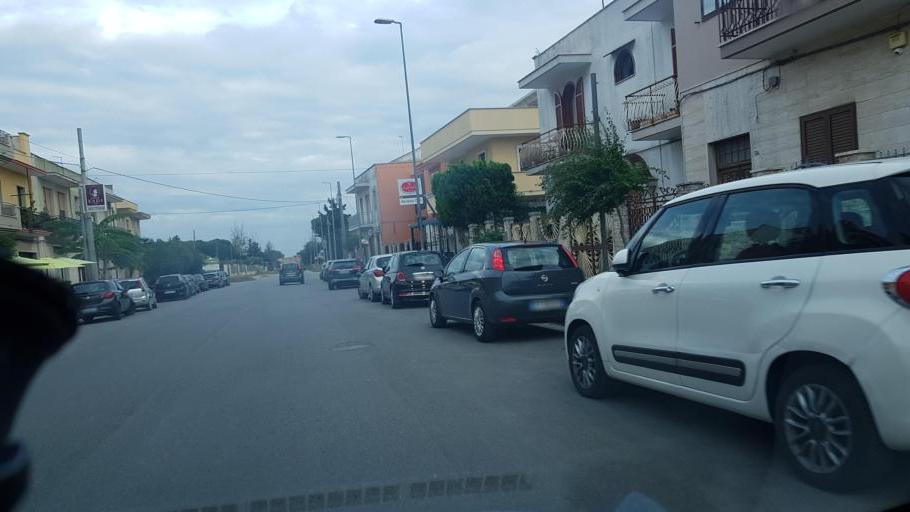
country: IT
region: Apulia
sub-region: Provincia di Brindisi
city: Francavilla Fontana
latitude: 40.5241
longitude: 17.5926
